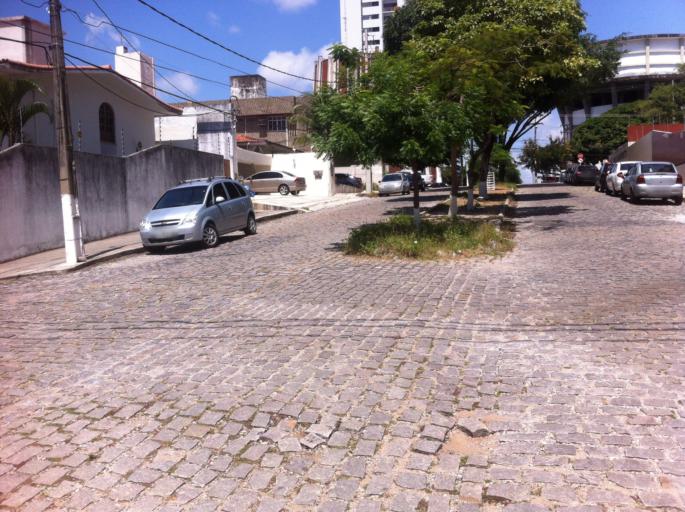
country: BR
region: Rio Grande do Norte
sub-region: Natal
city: Natal
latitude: -5.8206
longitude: -35.2144
